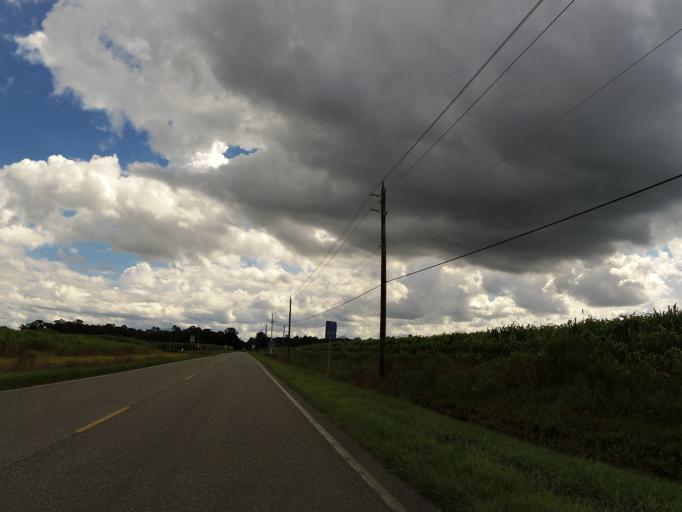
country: US
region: Florida
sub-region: Saint Johns County
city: Saint Augustine Shores
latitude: 29.7923
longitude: -81.4842
